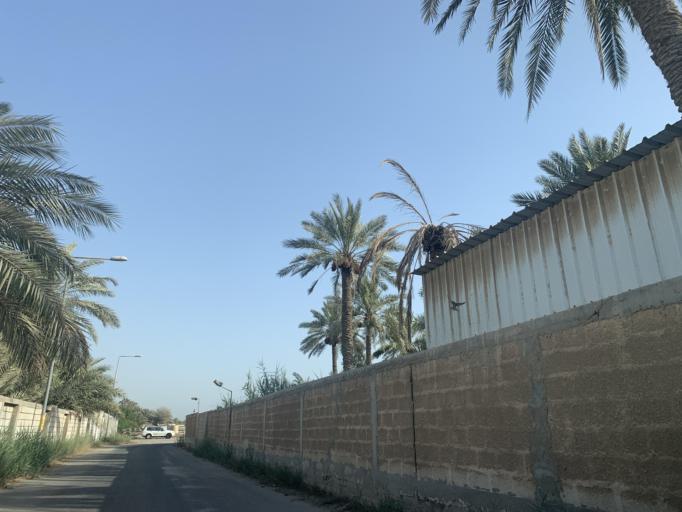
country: BH
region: Central Governorate
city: Madinat Hamad
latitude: 26.1925
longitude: 50.4579
